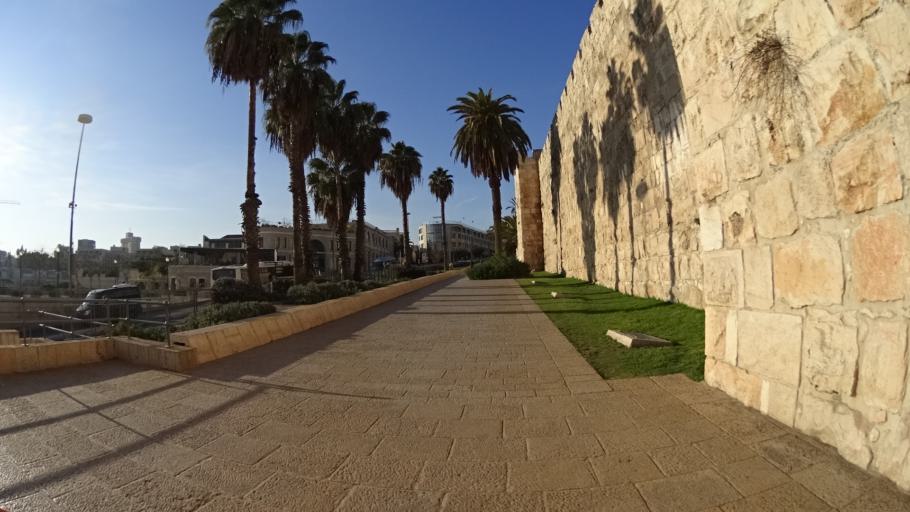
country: PS
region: West Bank
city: Old City
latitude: 31.7773
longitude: 35.2266
